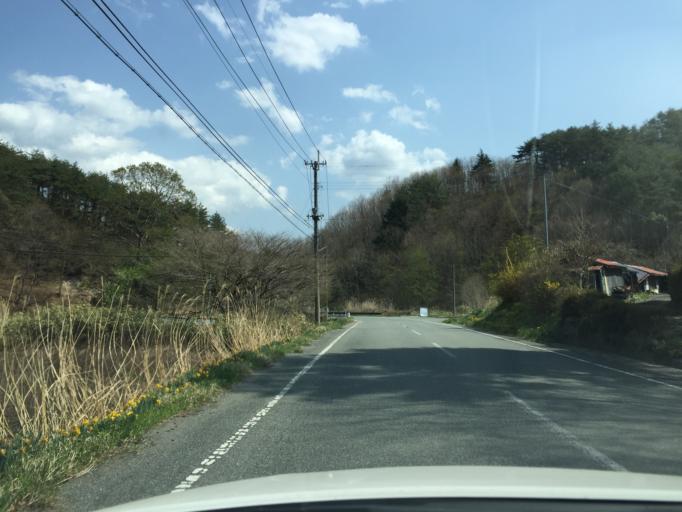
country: JP
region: Fukushima
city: Namie
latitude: 37.3652
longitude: 140.8089
